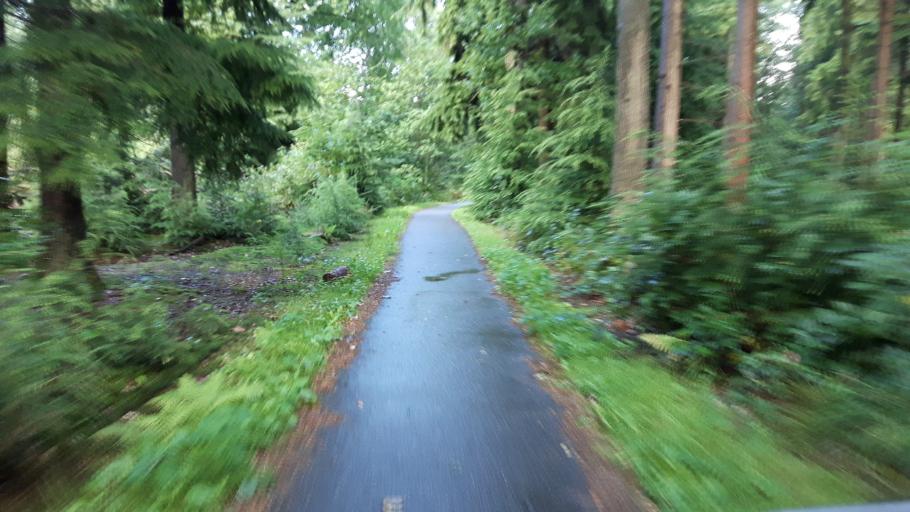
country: NL
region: Friesland
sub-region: Gemeente Smallingerland
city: Drachten
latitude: 53.0665
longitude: 6.1142
